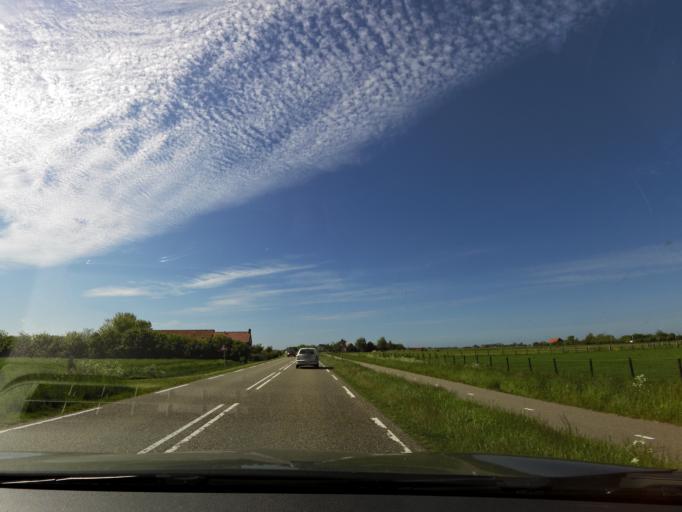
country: NL
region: Zeeland
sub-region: Schouwen-Duiveland
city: Scharendijke
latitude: 51.6654
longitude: 3.8847
